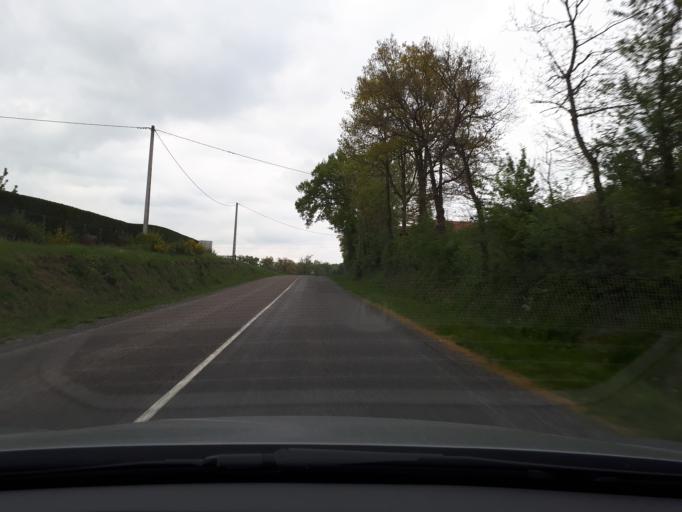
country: FR
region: Rhone-Alpes
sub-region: Departement de la Loire
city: Bellegarde-en-Forez
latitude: 45.6849
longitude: 4.3003
